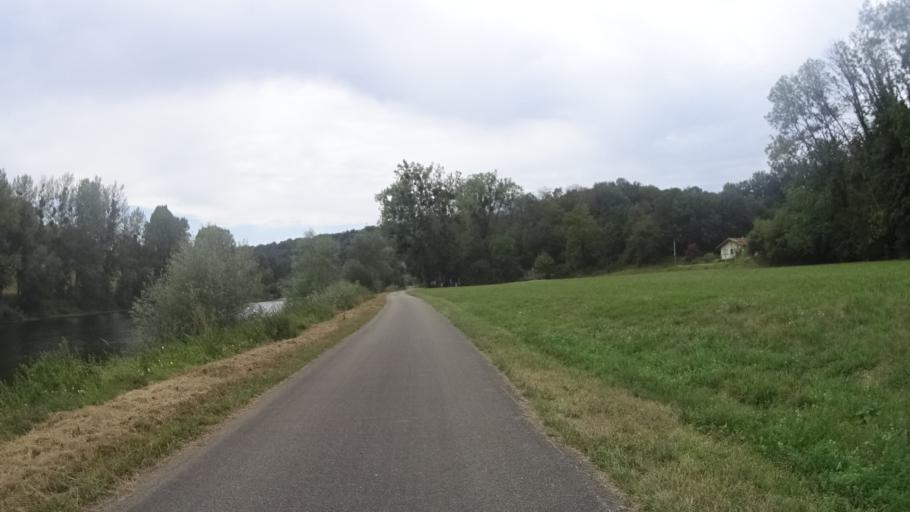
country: FR
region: Franche-Comte
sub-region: Departement du Doubs
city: Baume-les-Dames
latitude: 47.3416
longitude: 6.3355
